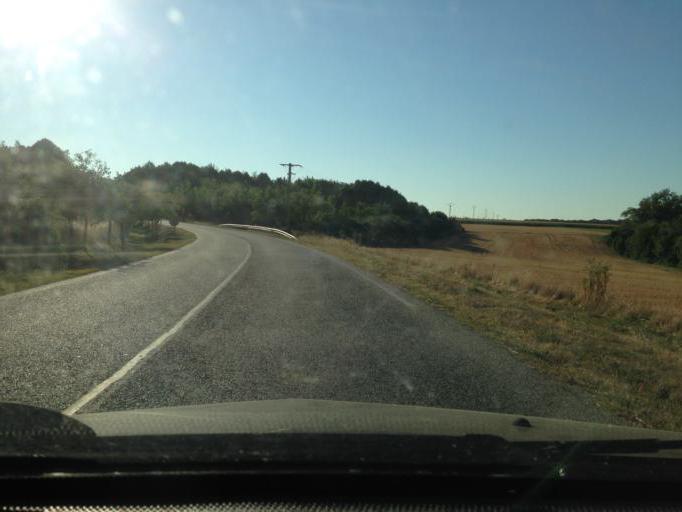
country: FR
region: Ile-de-France
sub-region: Departement des Yvelines
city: Chateaufort
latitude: 48.7304
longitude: 2.0796
